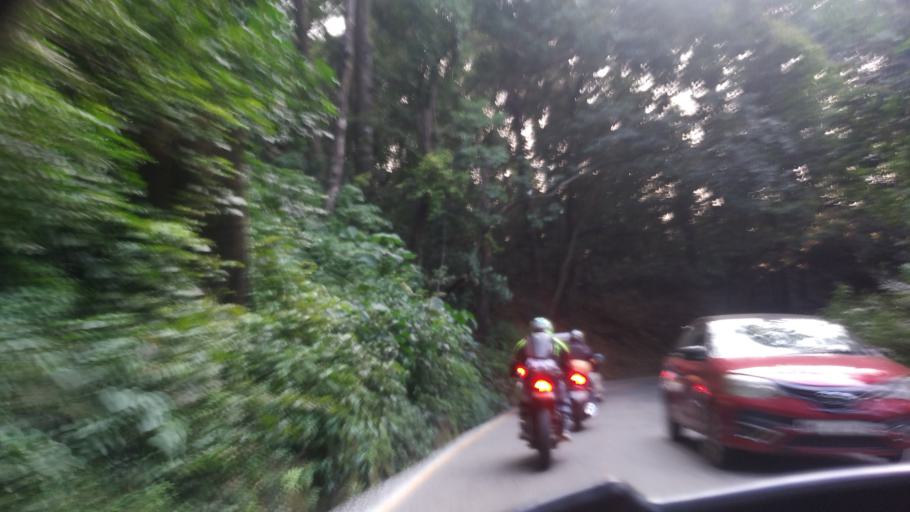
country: IN
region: Kerala
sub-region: Wayanad
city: Kalpetta
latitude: 11.5041
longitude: 76.0280
